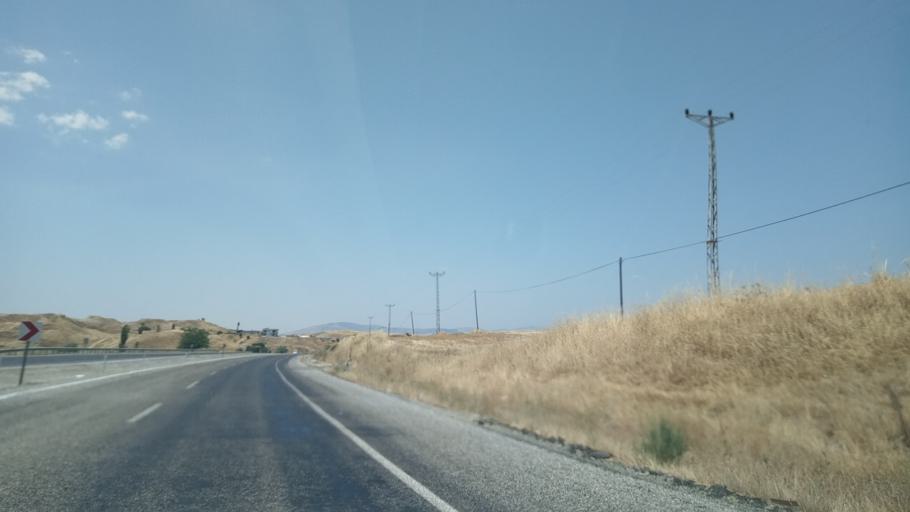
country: TR
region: Batman
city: Bekirhan
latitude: 38.1551
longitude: 41.3621
